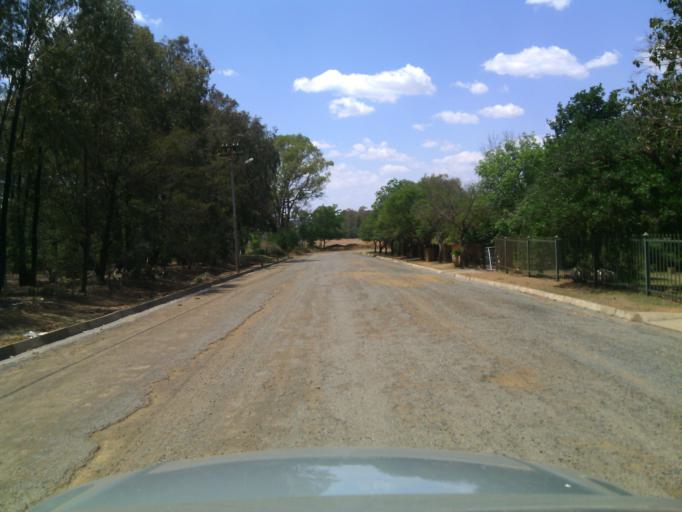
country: ZA
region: Orange Free State
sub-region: Xhariep District Municipality
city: Dewetsdorp
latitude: -29.5772
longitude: 26.6658
